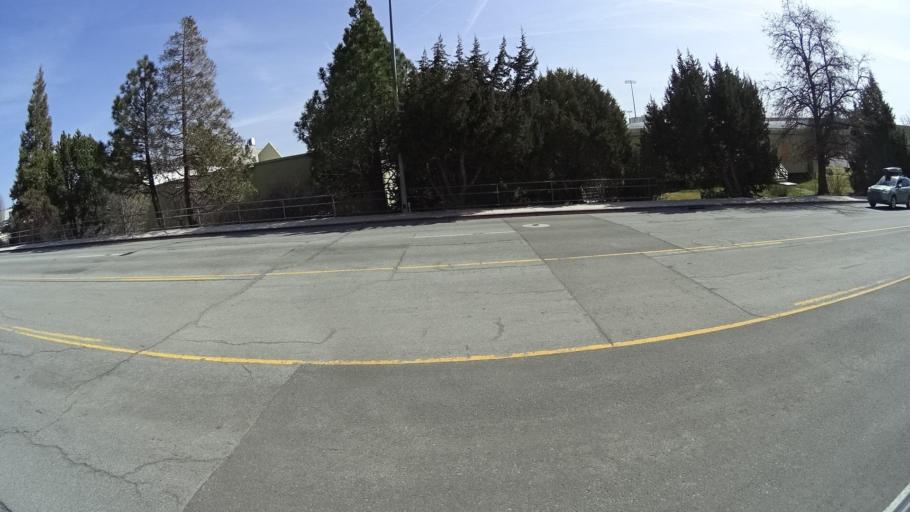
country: US
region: Nevada
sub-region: Washoe County
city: Reno
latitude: 39.5475
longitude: -119.8211
